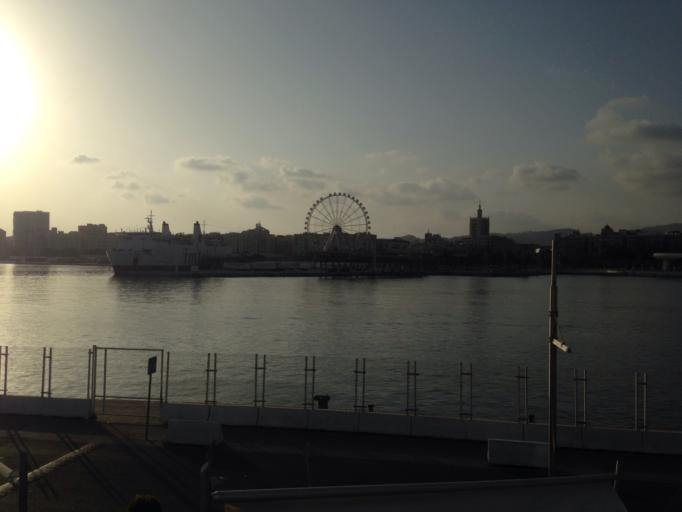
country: ES
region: Andalusia
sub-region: Provincia de Malaga
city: Malaga
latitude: 36.7146
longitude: -4.4148
